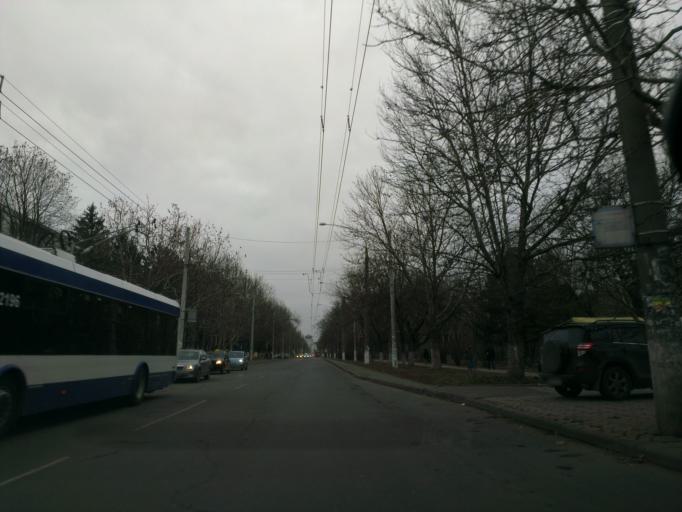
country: MD
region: Chisinau
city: Chisinau
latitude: 46.9788
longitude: 28.8547
